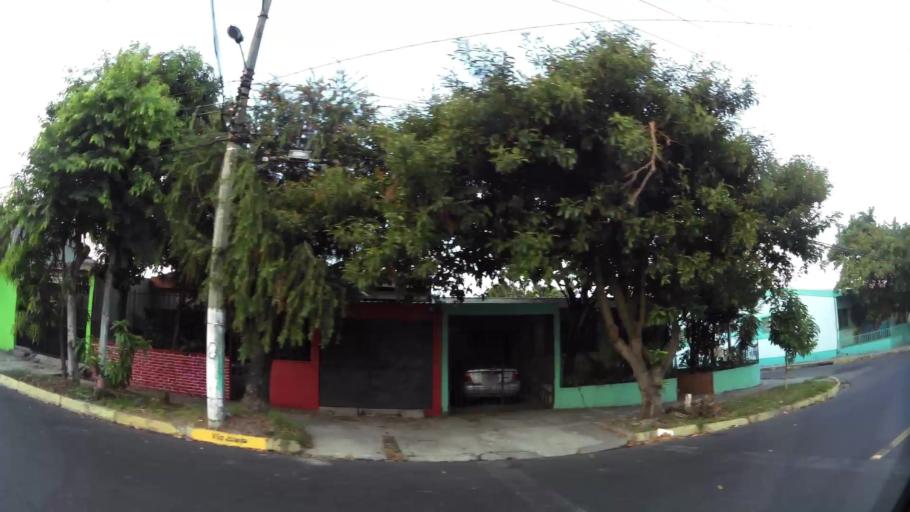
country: SV
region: San Salvador
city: Delgado
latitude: 13.7169
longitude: -89.1858
